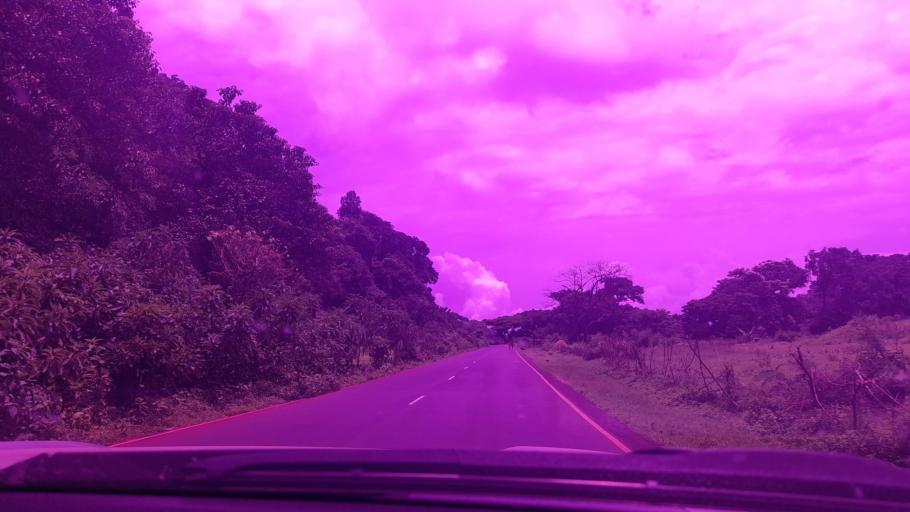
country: ET
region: Oromiya
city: Metu
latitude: 8.3339
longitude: 35.7458
